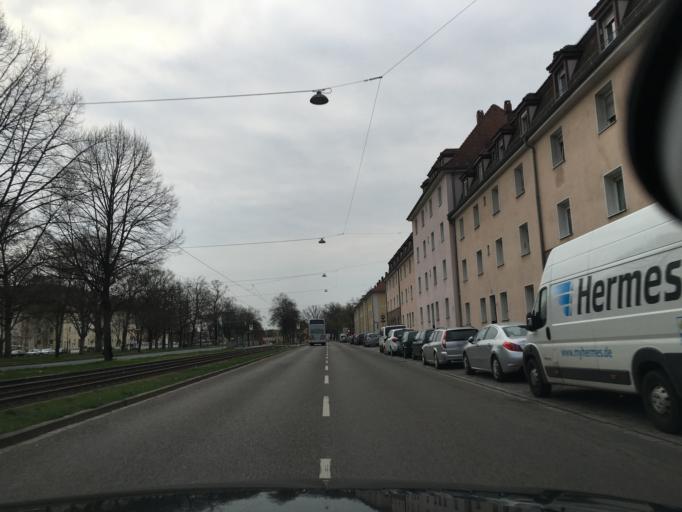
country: DE
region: Bavaria
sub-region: Regierungsbezirk Mittelfranken
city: Nuernberg
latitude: 49.4406
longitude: 11.1097
